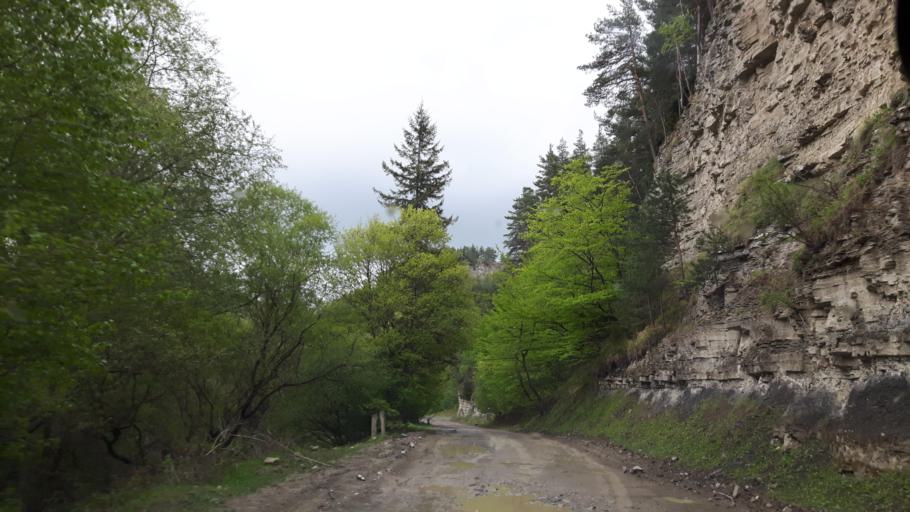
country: GE
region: Shida Kartli
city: Gori
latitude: 41.8604
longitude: 43.9578
